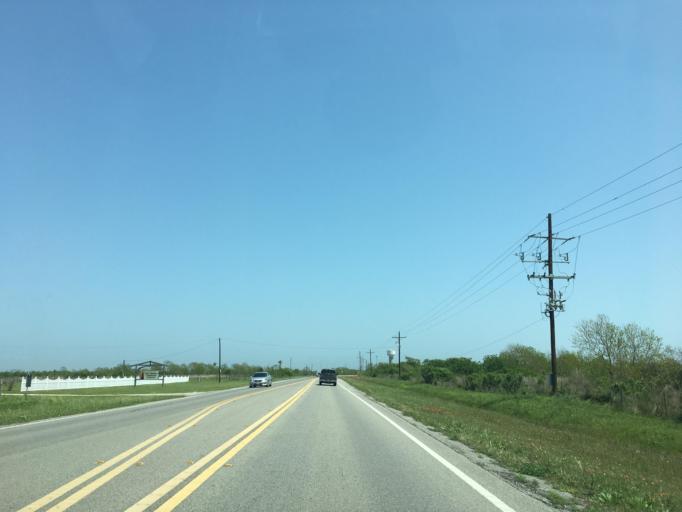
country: US
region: Texas
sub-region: Galveston County
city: Galveston
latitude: 29.4147
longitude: -94.7110
